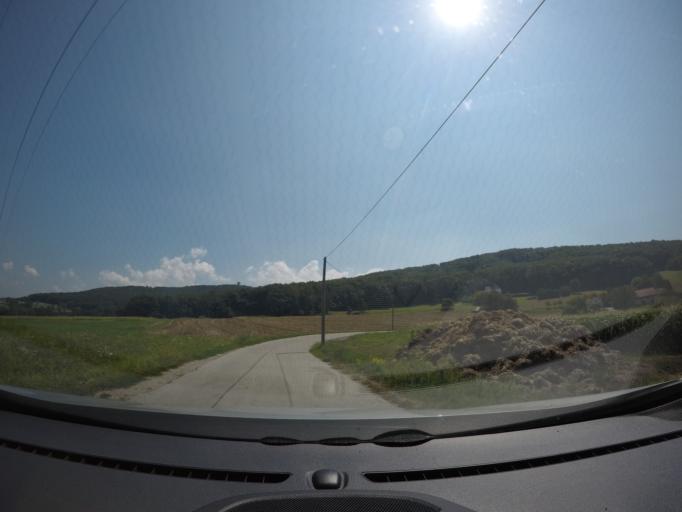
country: AT
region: Lower Austria
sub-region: Politischer Bezirk Sankt Polten
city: Maria-Anzbach
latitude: 48.2176
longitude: 15.9303
